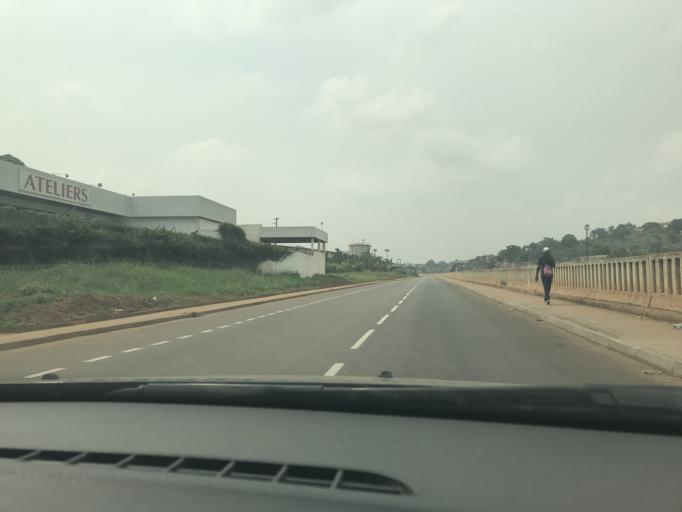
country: CM
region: Centre
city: Yaounde
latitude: 3.8465
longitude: 11.5160
